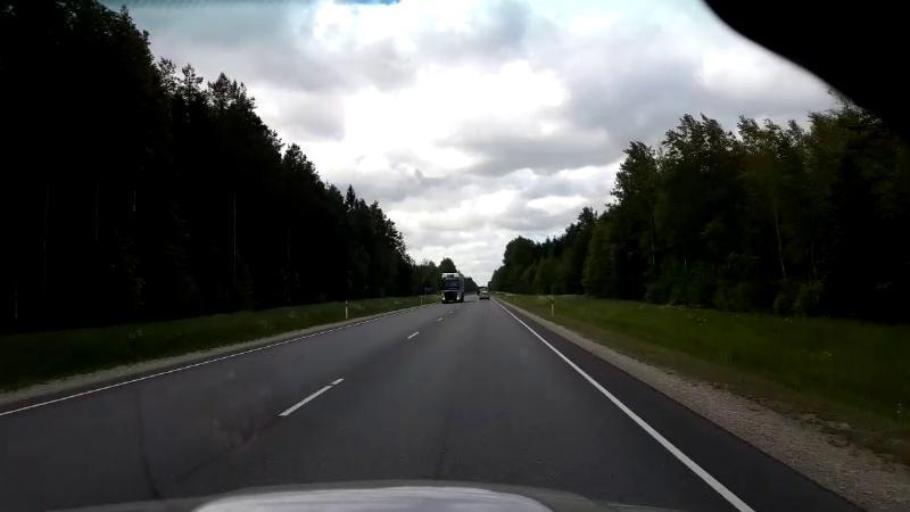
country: EE
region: Raplamaa
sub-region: Maerjamaa vald
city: Marjamaa
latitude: 58.7995
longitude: 24.4128
